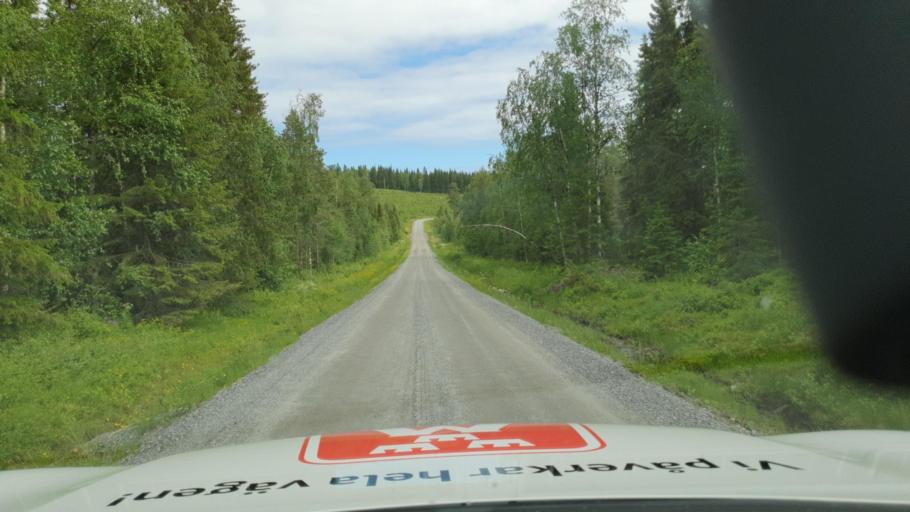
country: SE
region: Vaesterbotten
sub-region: Skelleftea Kommun
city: Langsele
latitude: 64.6444
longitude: 20.2787
